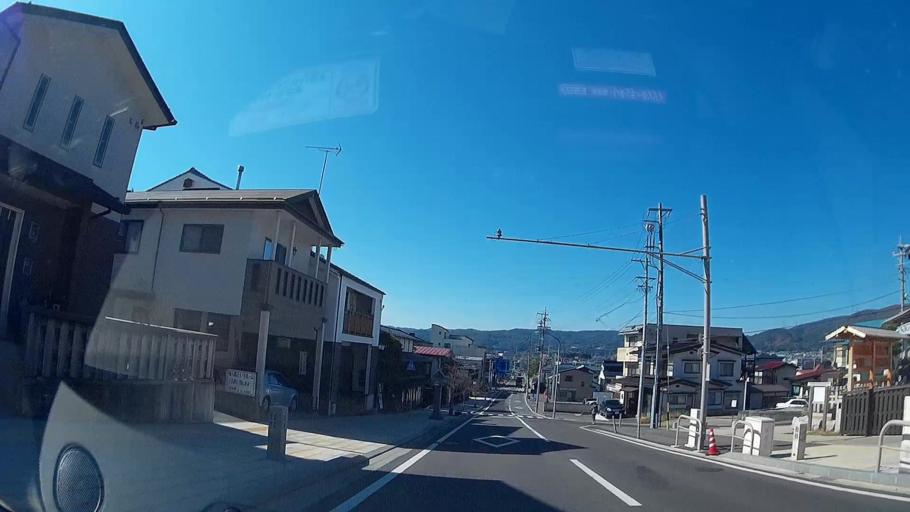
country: JP
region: Nagano
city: Suwa
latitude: 36.0747
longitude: 138.0883
